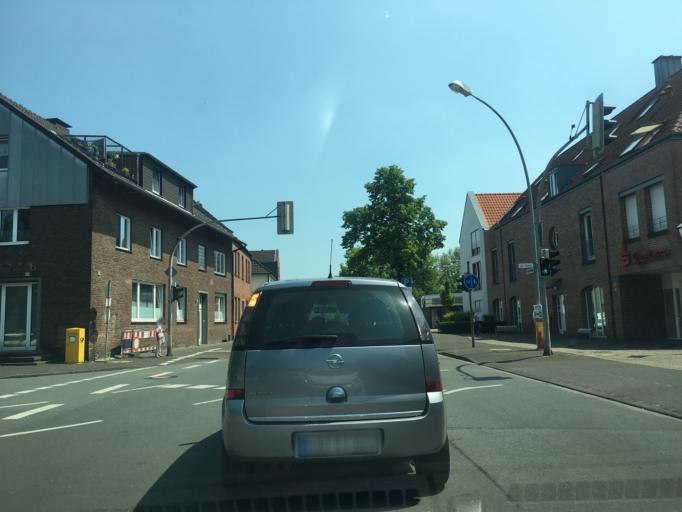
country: DE
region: North Rhine-Westphalia
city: Olfen
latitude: 51.7090
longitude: 7.3798
